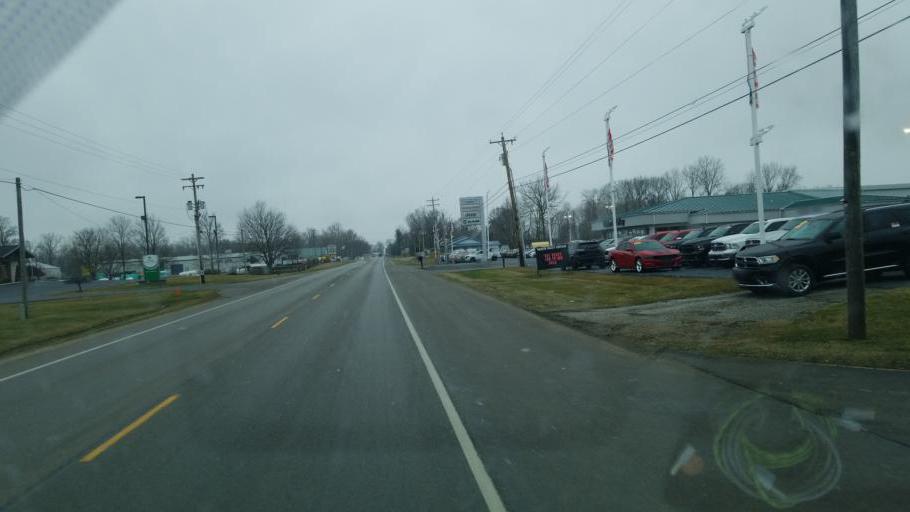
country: US
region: Indiana
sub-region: Wabash County
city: Wabash
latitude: 40.7773
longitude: -85.8196
